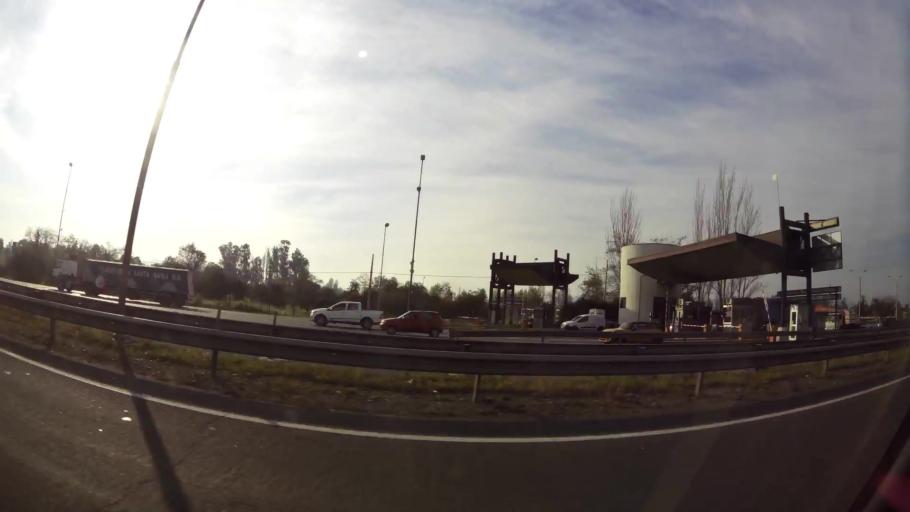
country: CL
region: Santiago Metropolitan
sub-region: Provincia de Talagante
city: Penaflor
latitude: -33.6071
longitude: -70.8506
